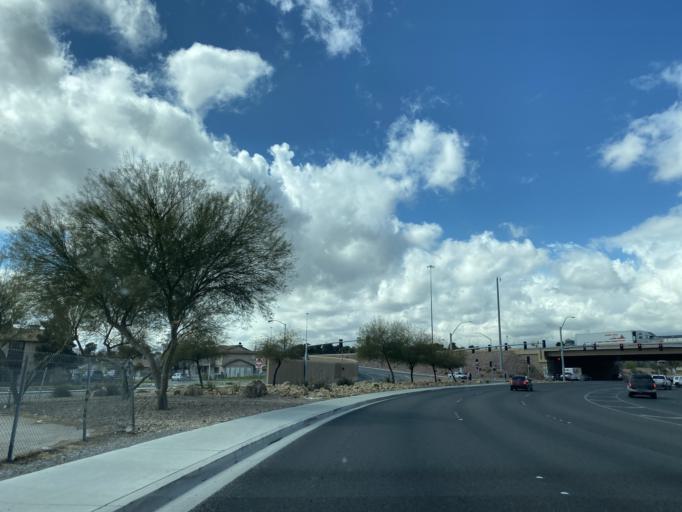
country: US
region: Nevada
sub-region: Clark County
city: North Las Vegas
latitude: 36.1962
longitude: -115.1370
